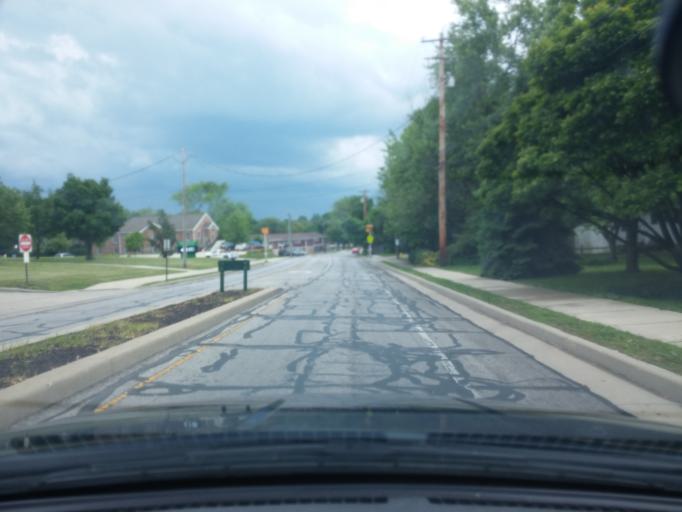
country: US
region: Indiana
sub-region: Tippecanoe County
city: West Lafayette
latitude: 40.4374
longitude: -86.9063
